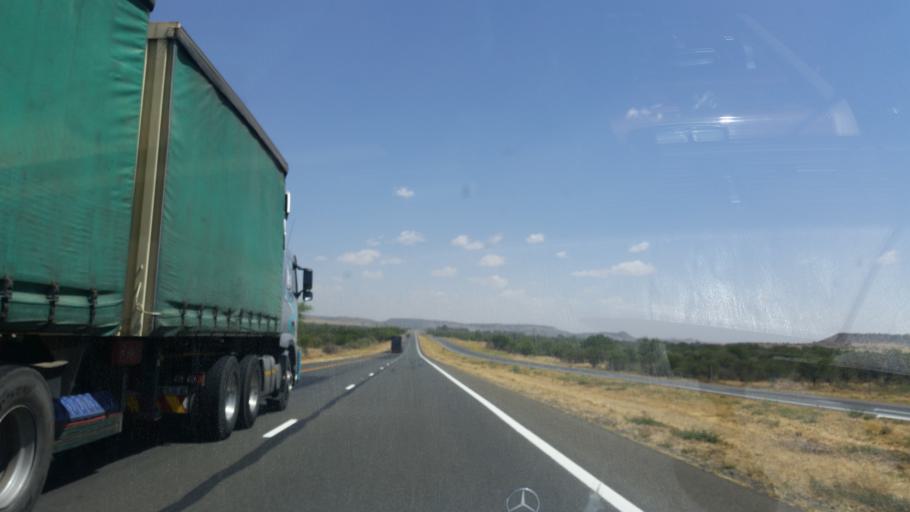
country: ZA
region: Orange Free State
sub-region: Mangaung Metropolitan Municipality
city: Bloemfontein
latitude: -28.9568
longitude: 26.3781
